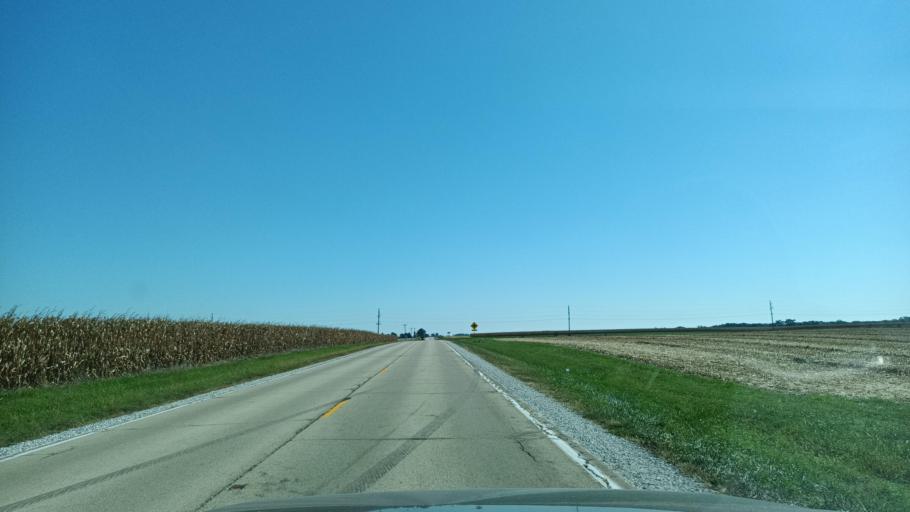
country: US
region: Illinois
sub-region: Peoria County
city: Elmwood
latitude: 40.9022
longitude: -89.9697
